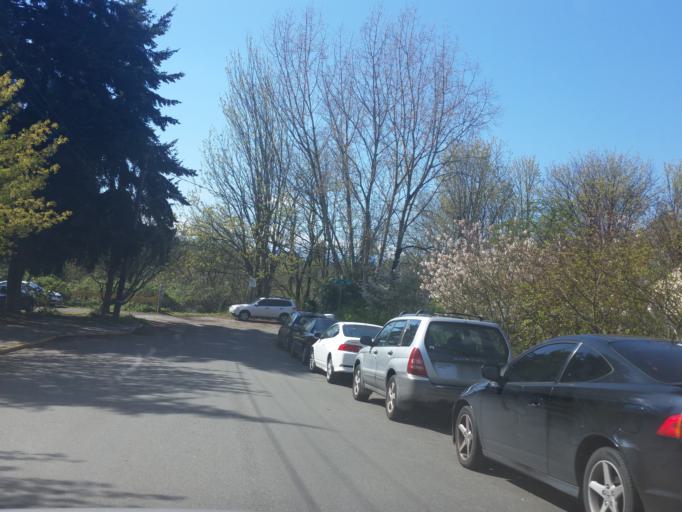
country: US
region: Washington
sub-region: King County
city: Shoreline
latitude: 47.7070
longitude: -122.3613
